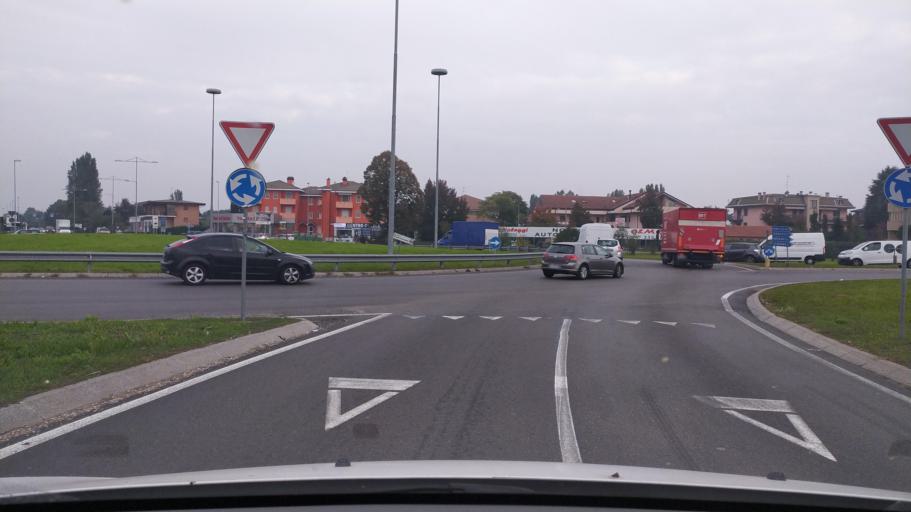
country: IT
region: Lombardy
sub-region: Citta metropolitana di Milano
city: Vittuone
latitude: 45.4812
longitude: 8.9494
